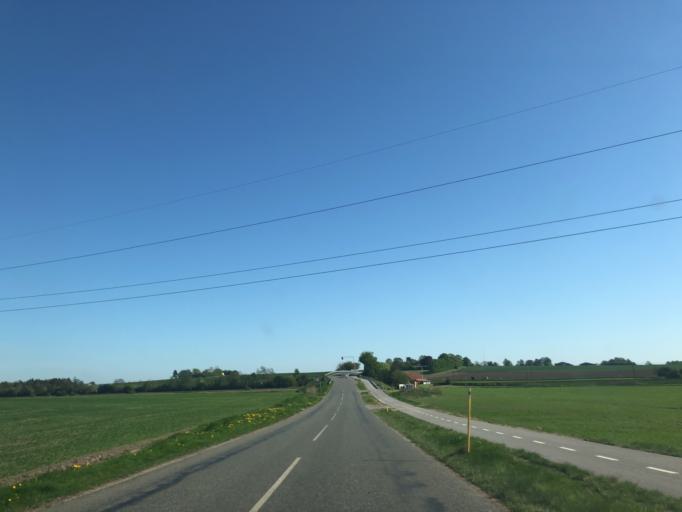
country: DK
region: Zealand
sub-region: Ringsted Kommune
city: Ringsted
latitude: 55.4401
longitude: 11.7271
